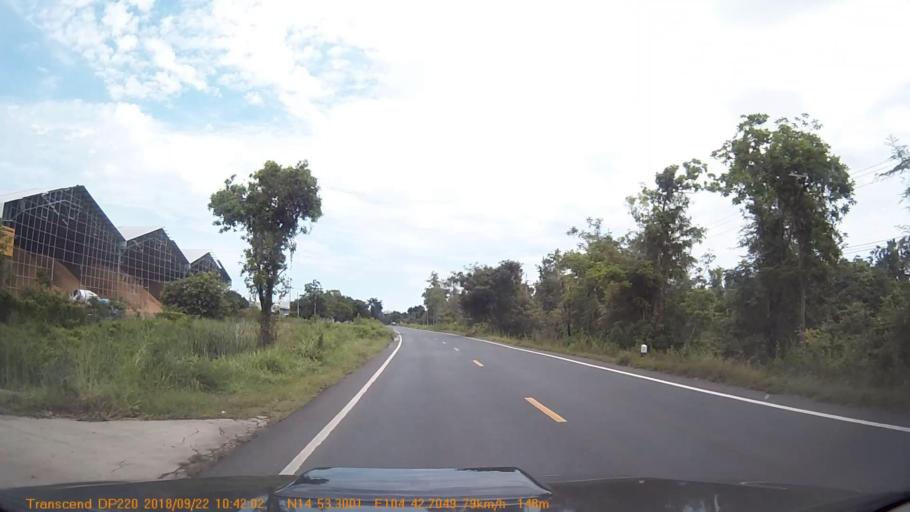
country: TH
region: Sisaket
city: Non Kho
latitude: 14.8884
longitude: 104.7118
